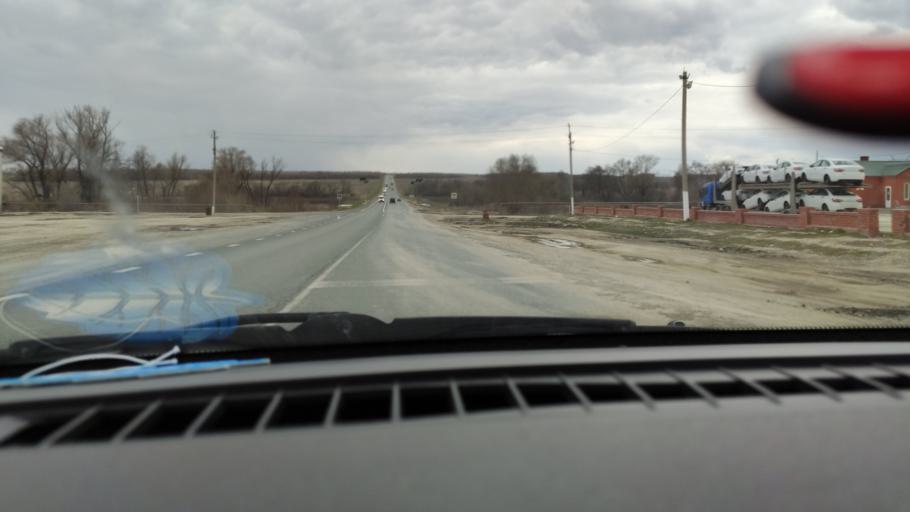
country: RU
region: Saratov
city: Sinodskoye
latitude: 51.9175
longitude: 46.5583
